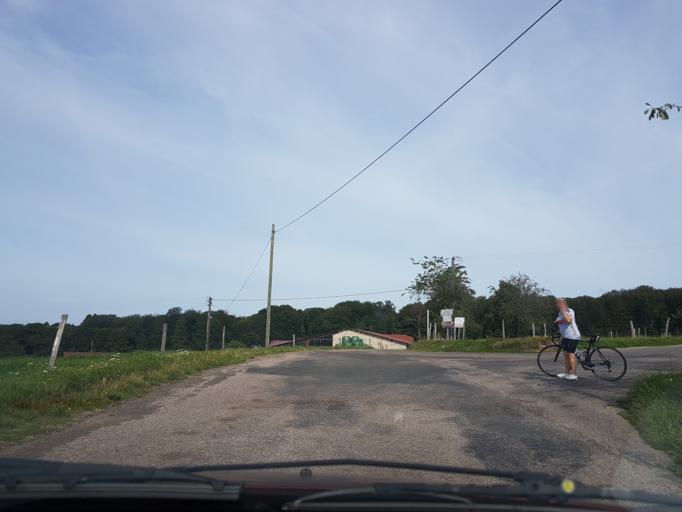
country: FR
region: Franche-Comte
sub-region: Departement de la Haute-Saone
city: Fougerolles
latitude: 47.8697
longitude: 6.4727
